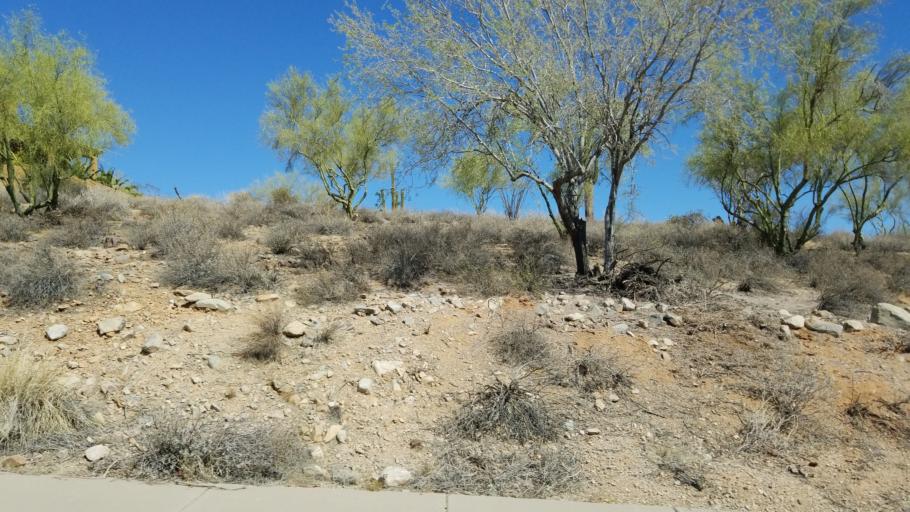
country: US
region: Arizona
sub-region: Maricopa County
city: Fountain Hills
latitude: 33.6132
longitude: -111.7379
